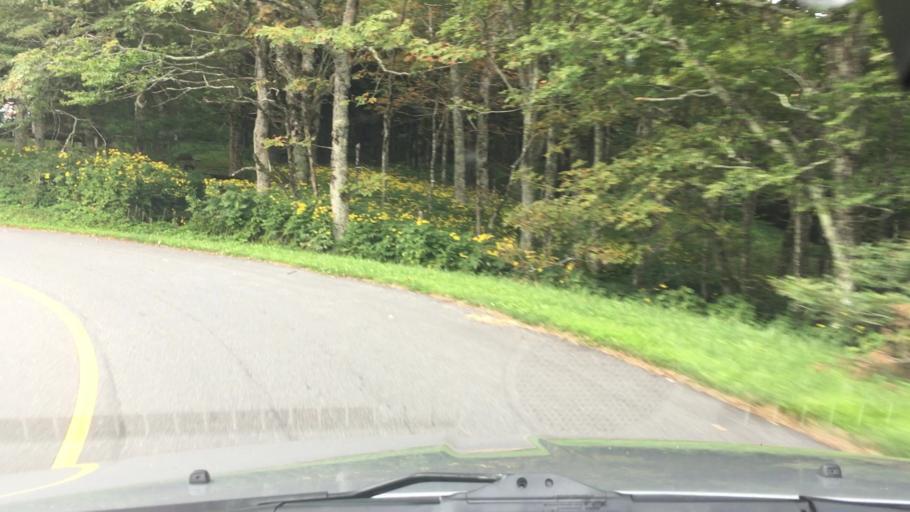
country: US
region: North Carolina
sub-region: Buncombe County
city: Swannanoa
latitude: 35.7001
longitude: -82.3926
